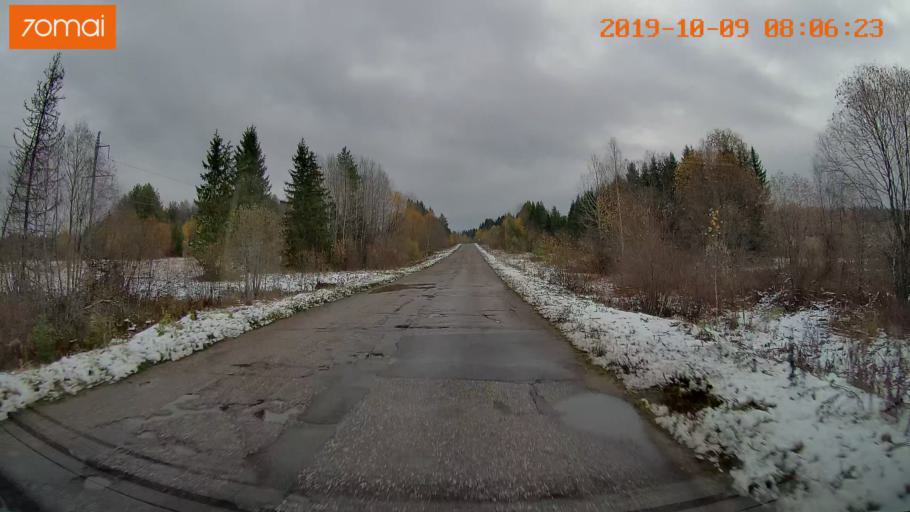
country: RU
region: Jaroslavl
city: Kukoboy
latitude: 58.6933
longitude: 40.0617
